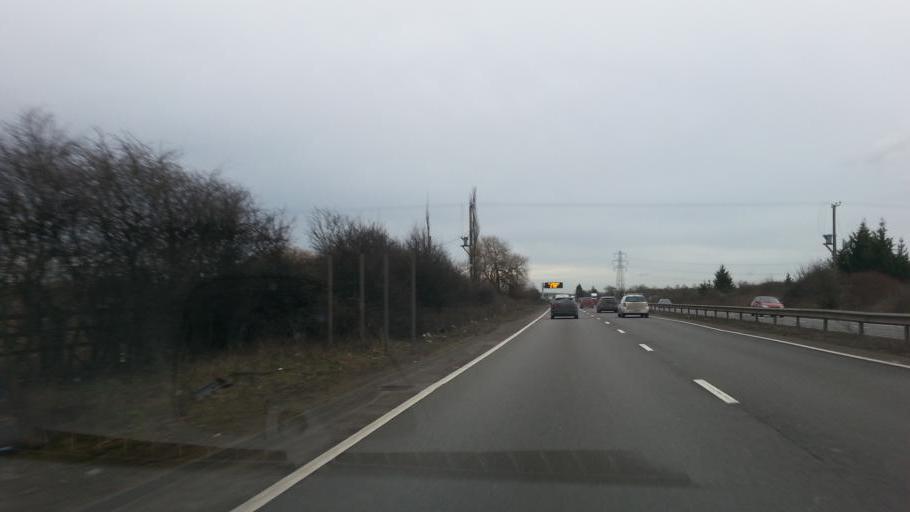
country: GB
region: England
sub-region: Cambridgeshire
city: Buckden
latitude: 52.3323
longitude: -0.2750
